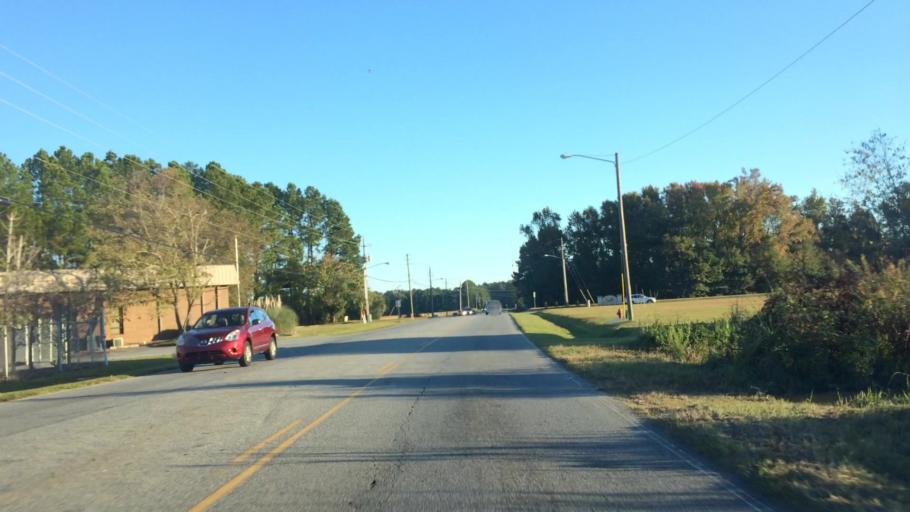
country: US
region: North Carolina
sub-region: Pitt County
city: Summerfield
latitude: 35.5609
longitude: -77.3865
